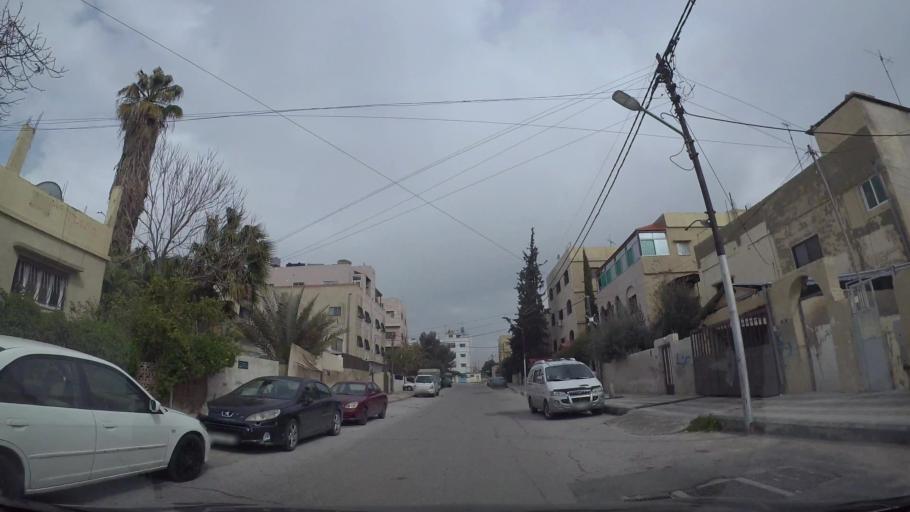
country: JO
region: Amman
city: Amman
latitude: 31.9711
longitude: 35.9344
